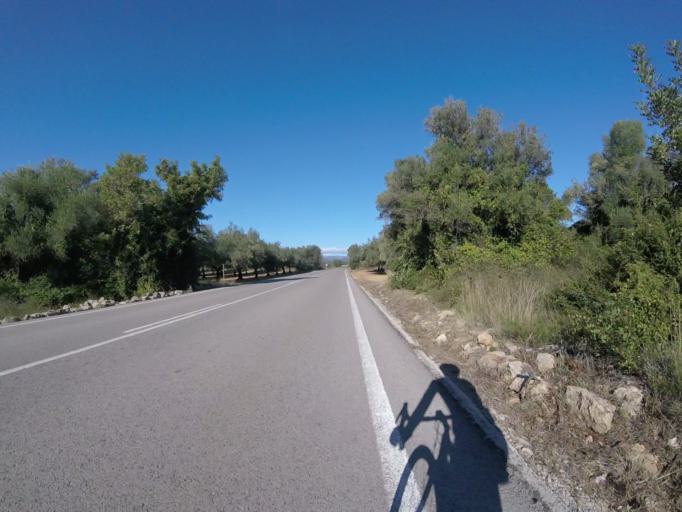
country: ES
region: Valencia
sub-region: Provincia de Castello
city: Cervera del Maestre
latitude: 40.4765
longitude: 0.2225
